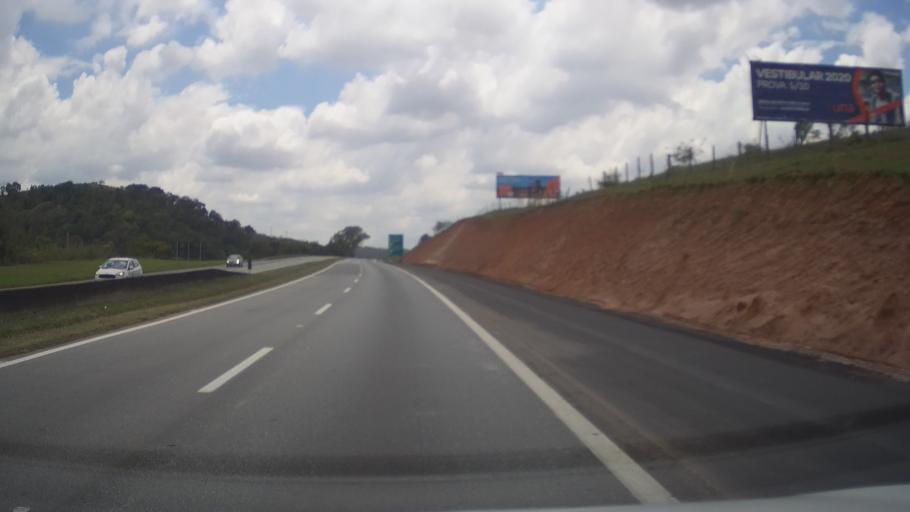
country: BR
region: Minas Gerais
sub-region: Tres Coracoes
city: Tres Coracoes
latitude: -21.6823
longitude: -45.3429
